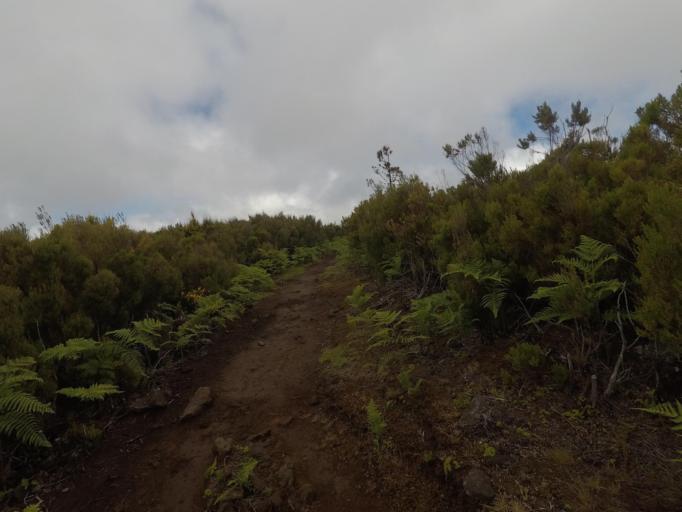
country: PT
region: Madeira
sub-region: Calheta
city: Arco da Calheta
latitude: 32.7744
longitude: -17.1326
